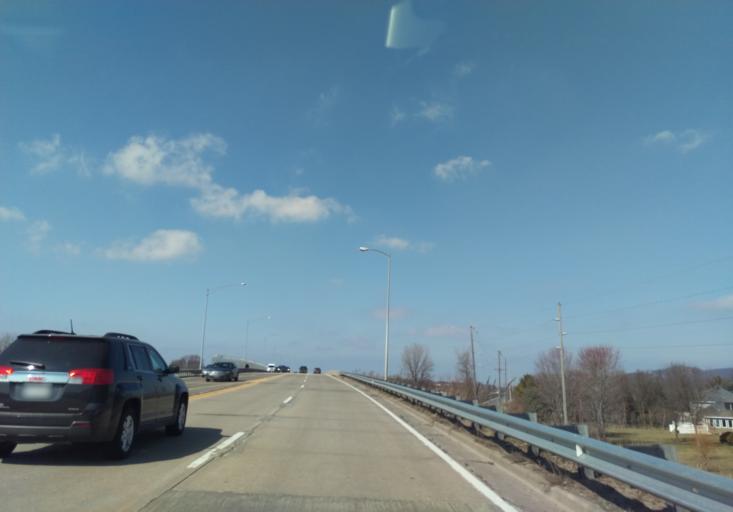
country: US
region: Wisconsin
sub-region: La Crosse County
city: La Crosse
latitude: 43.7603
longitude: -91.2062
